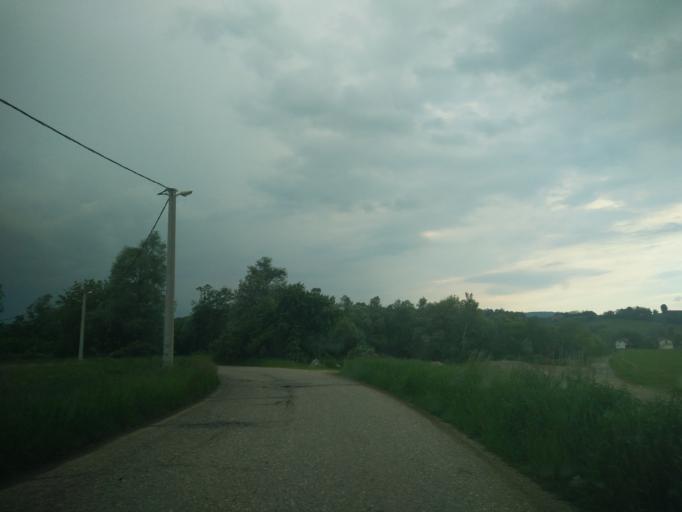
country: BA
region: Republika Srpska
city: Prijedor
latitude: 44.9253
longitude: 16.6980
